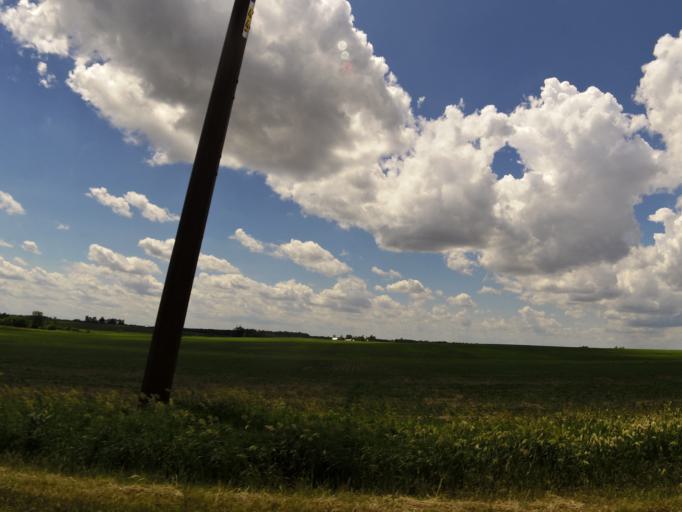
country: US
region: Iowa
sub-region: Buchanan County
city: Independence
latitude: 42.5580
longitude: -91.9049
